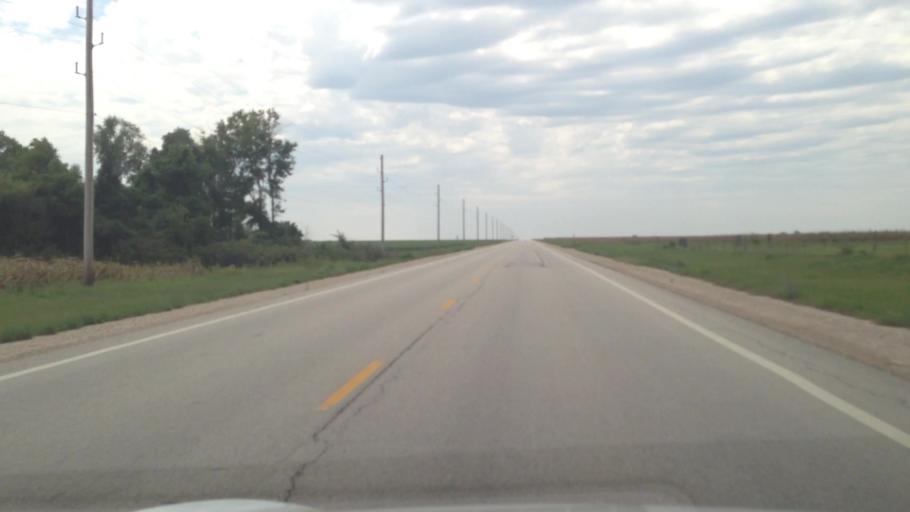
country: US
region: Kansas
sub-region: Anderson County
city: Garnett
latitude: 38.0643
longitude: -95.1694
